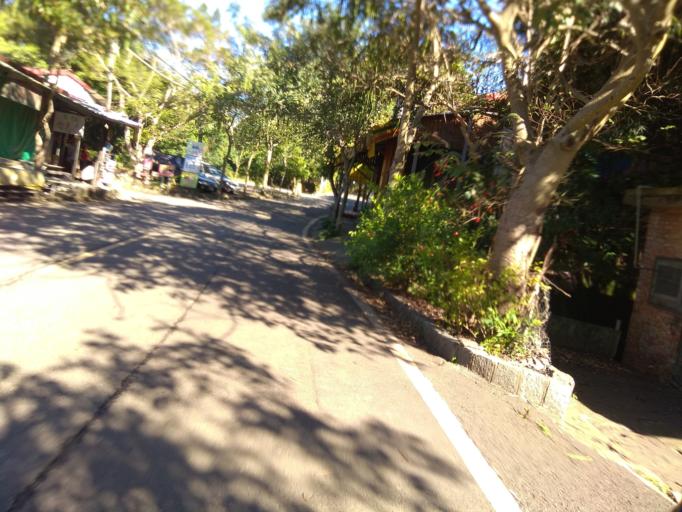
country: TW
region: Taiwan
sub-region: Hsinchu
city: Zhubei
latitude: 24.8561
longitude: 121.1053
